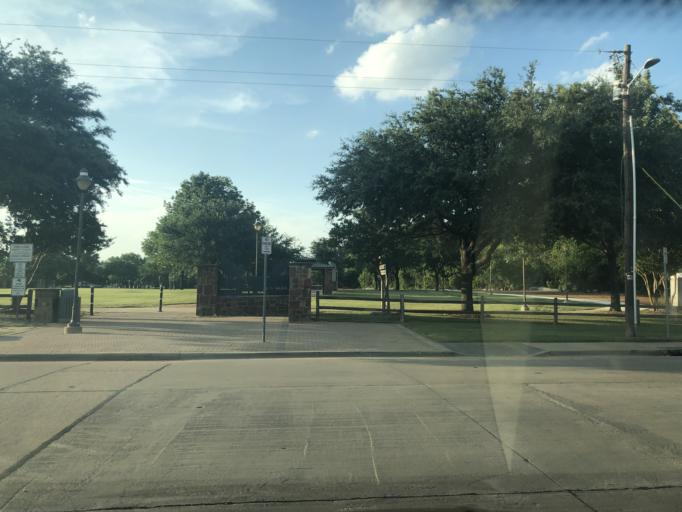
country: US
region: Texas
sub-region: Dallas County
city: Irving
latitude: 32.7974
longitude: -96.9555
